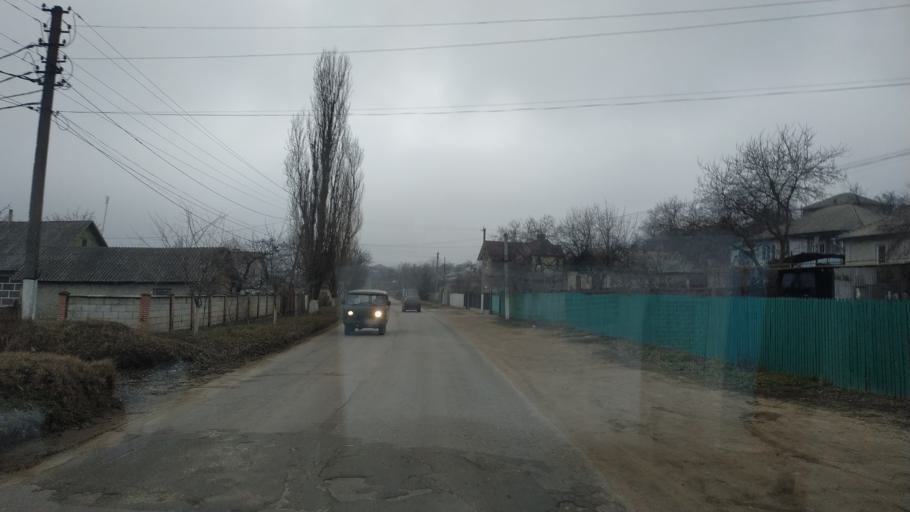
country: MD
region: Laloveni
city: Ialoveni
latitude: 46.9068
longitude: 28.6803
